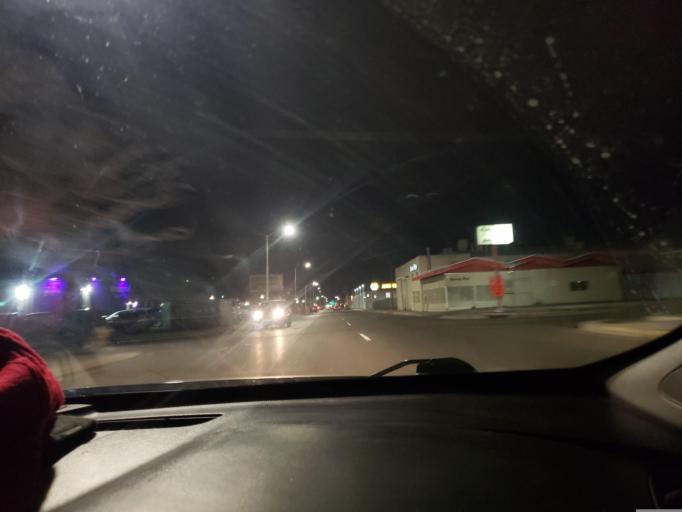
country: US
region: New Mexico
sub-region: Bernalillo County
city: Albuquerque
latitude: 35.0972
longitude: -106.6466
